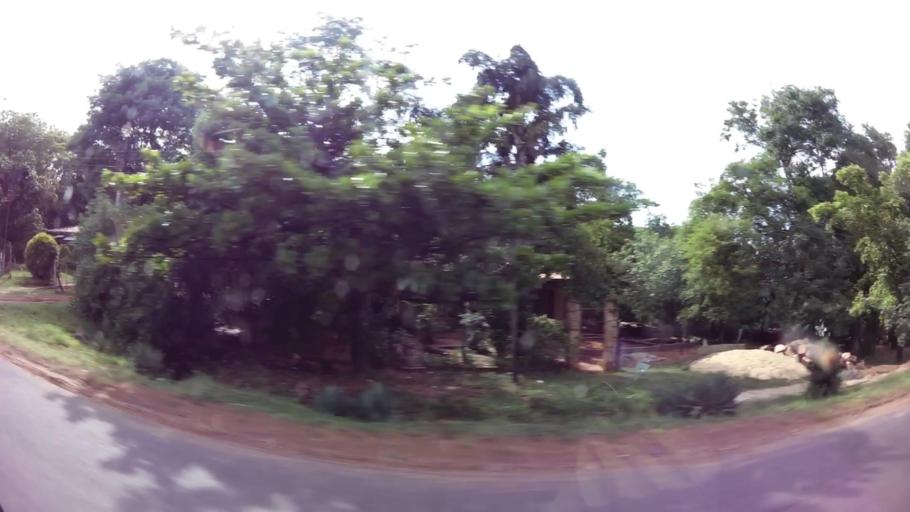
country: PY
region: Central
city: Limpio
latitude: -25.1550
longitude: -57.4630
